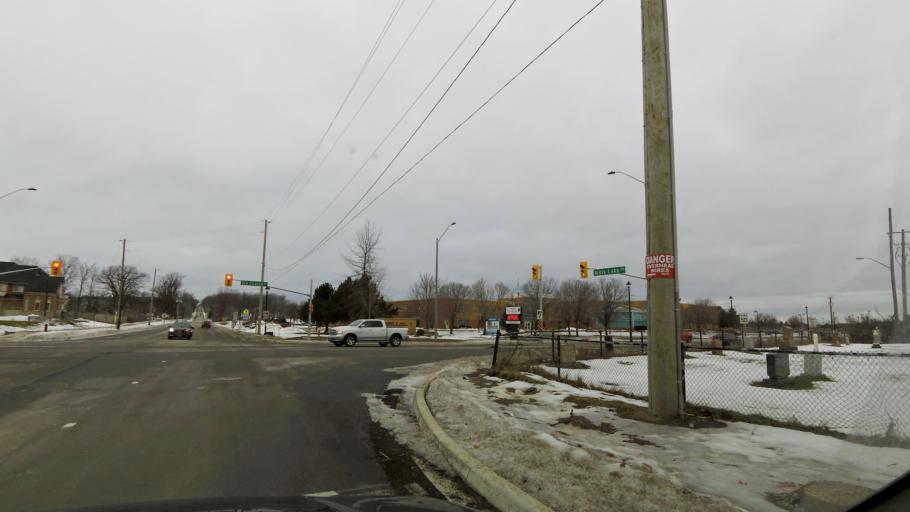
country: CA
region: Ontario
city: Brampton
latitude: 43.8786
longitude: -79.8549
